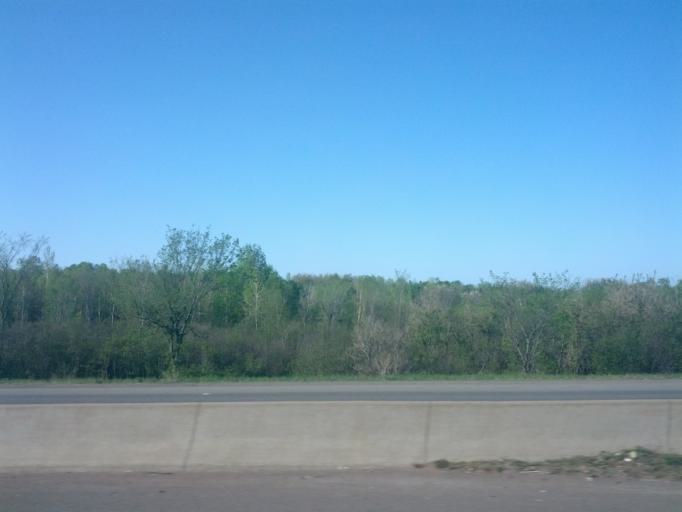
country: CA
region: New Brunswick
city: Moncton
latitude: 46.1135
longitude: -64.8109
